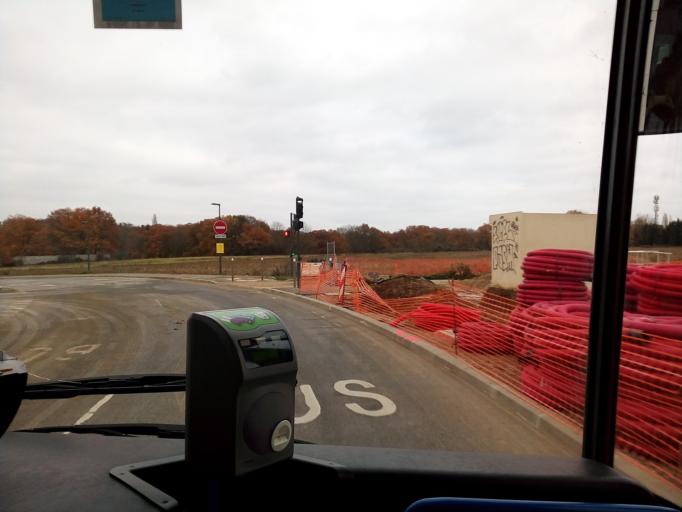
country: FR
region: Ile-de-France
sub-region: Departement de l'Essonne
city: Bures-sur-Yvette
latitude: 48.7119
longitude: 2.1751
